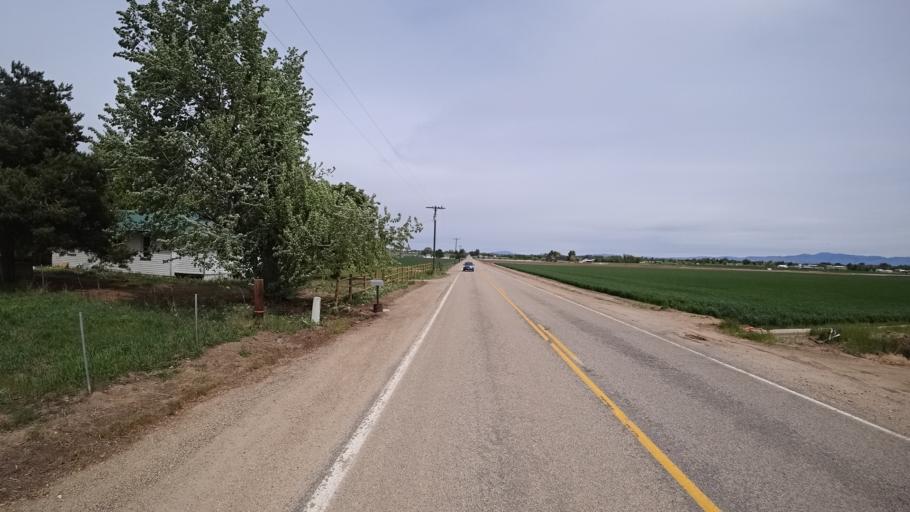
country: US
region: Idaho
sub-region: Ada County
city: Kuna
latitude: 43.5394
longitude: -116.4737
